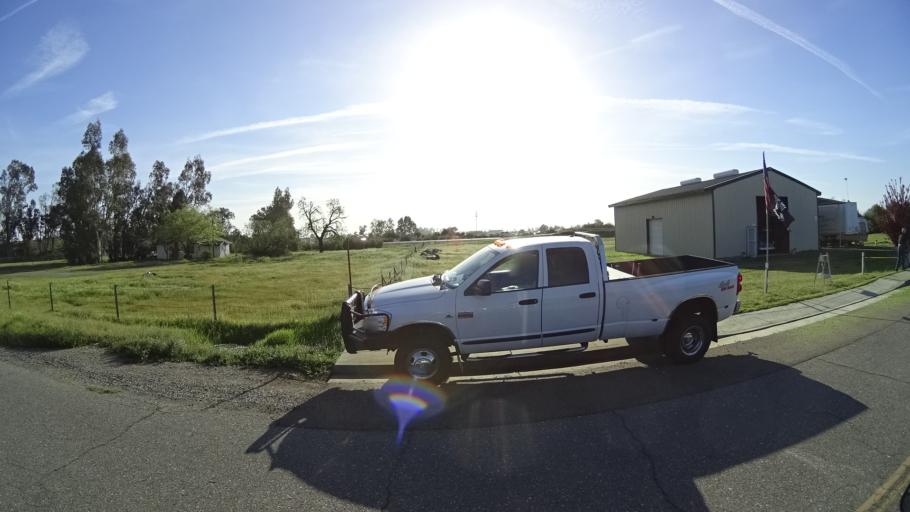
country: US
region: California
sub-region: Glenn County
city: Orland
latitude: 39.7393
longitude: -122.2076
